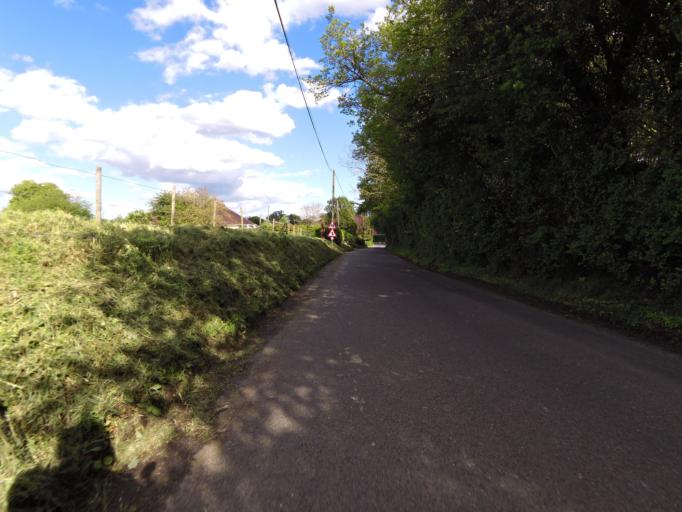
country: GB
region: England
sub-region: Suffolk
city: Woolpit
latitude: 52.2217
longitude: 0.8636
